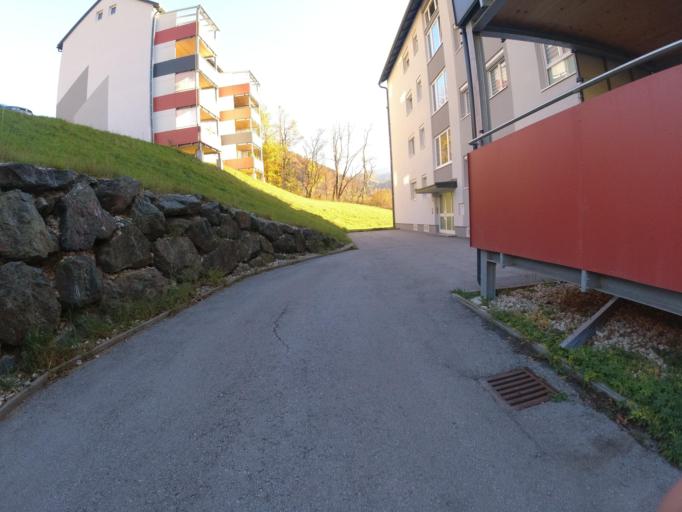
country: AT
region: Carinthia
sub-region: Politischer Bezirk Volkermarkt
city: Bad Eisenkappel
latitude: 46.4897
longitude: 14.5928
